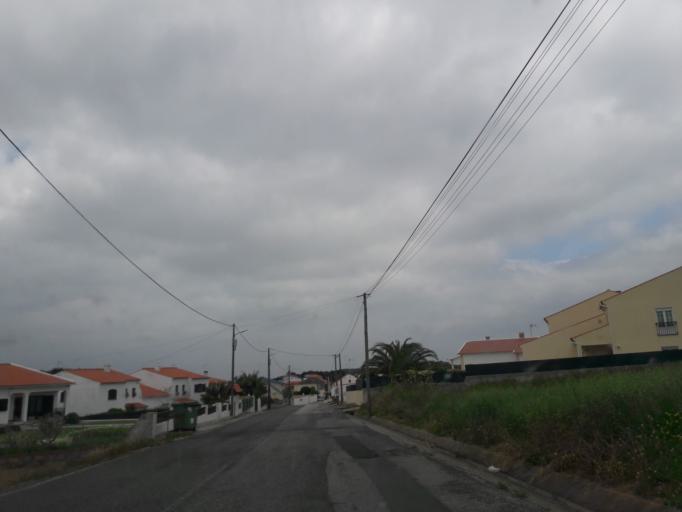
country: PT
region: Leiria
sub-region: Peniche
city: Atouguia da Baleia
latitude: 39.3483
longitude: -9.2861
